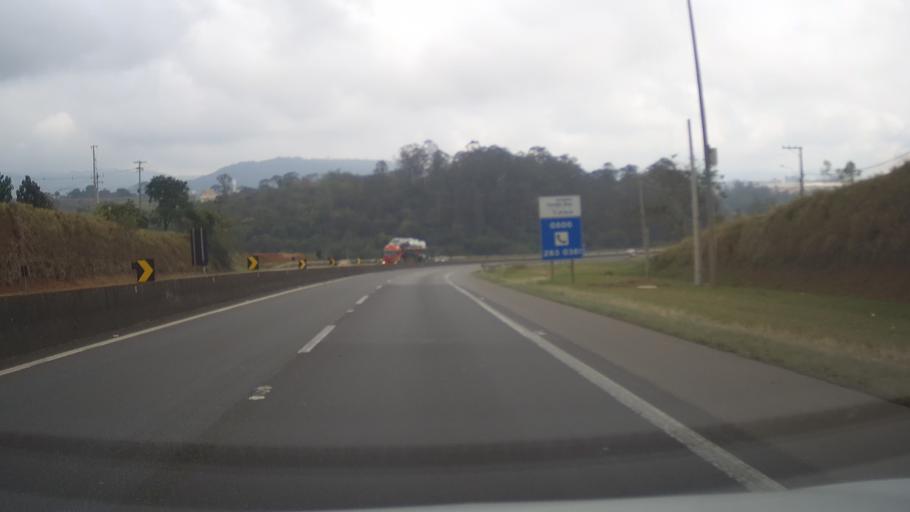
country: BR
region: Minas Gerais
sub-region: Extrema
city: Extrema
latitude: -22.8526
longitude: -46.3373
